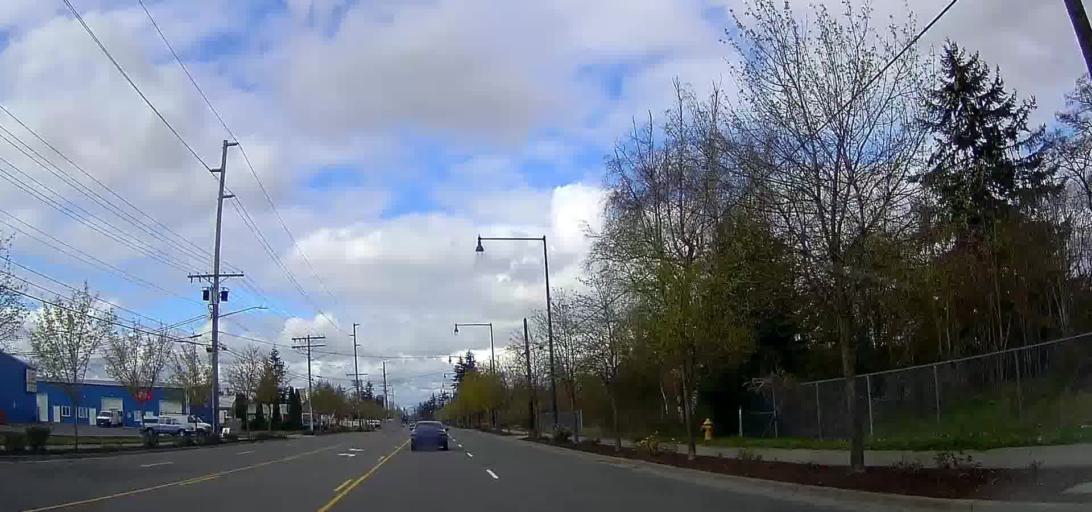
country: US
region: Washington
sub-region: Snohomish County
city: Smokey Point
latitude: 48.1278
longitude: -122.1836
